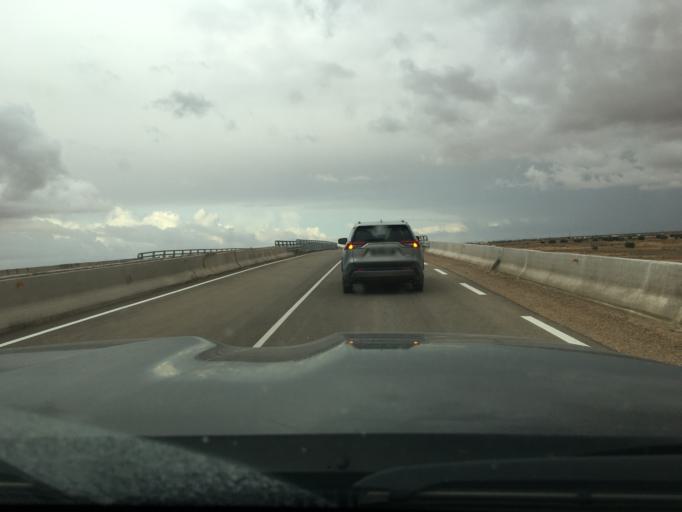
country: TN
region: Madanin
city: Medenine
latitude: 33.2989
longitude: 10.6087
